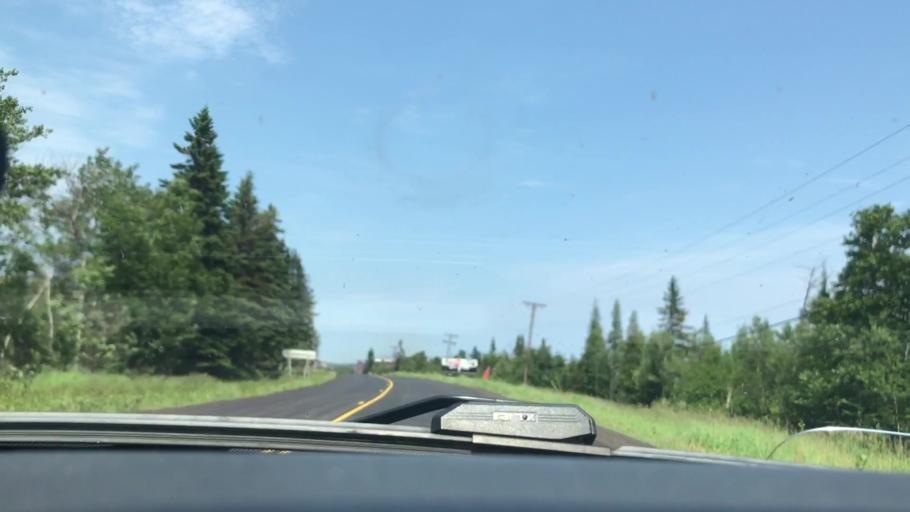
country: US
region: Minnesota
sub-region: Lake County
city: Silver Bay
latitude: 47.2728
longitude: -91.2775
